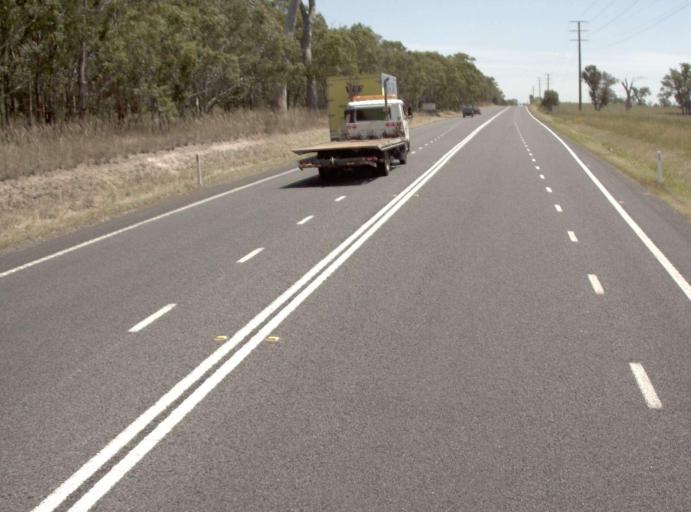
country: AU
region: Victoria
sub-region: Latrobe
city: Traralgon
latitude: -38.1751
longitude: 146.6517
